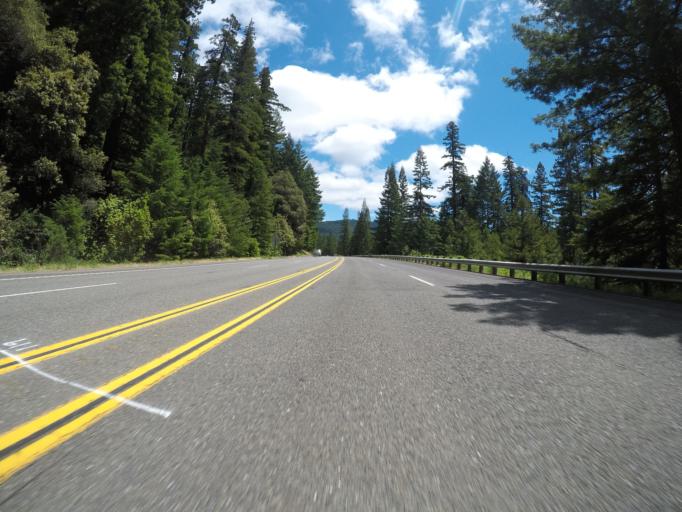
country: US
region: California
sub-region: Humboldt County
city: Redway
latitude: 40.2758
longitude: -123.8829
